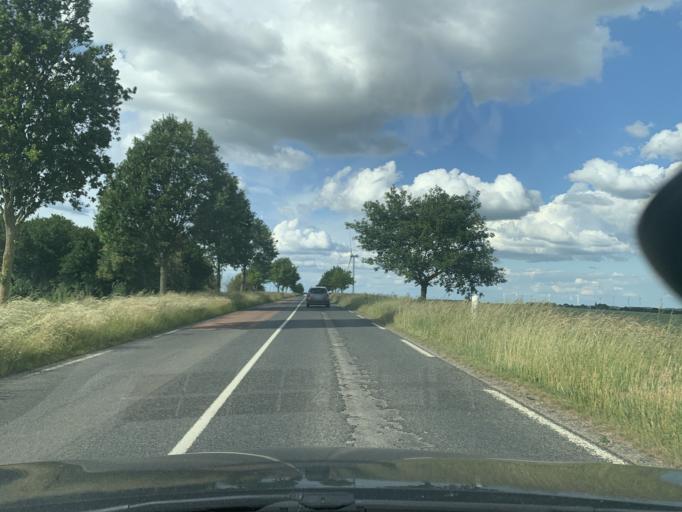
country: FR
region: Picardie
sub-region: Departement de la Somme
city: Moislains
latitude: 50.0116
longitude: 3.0267
